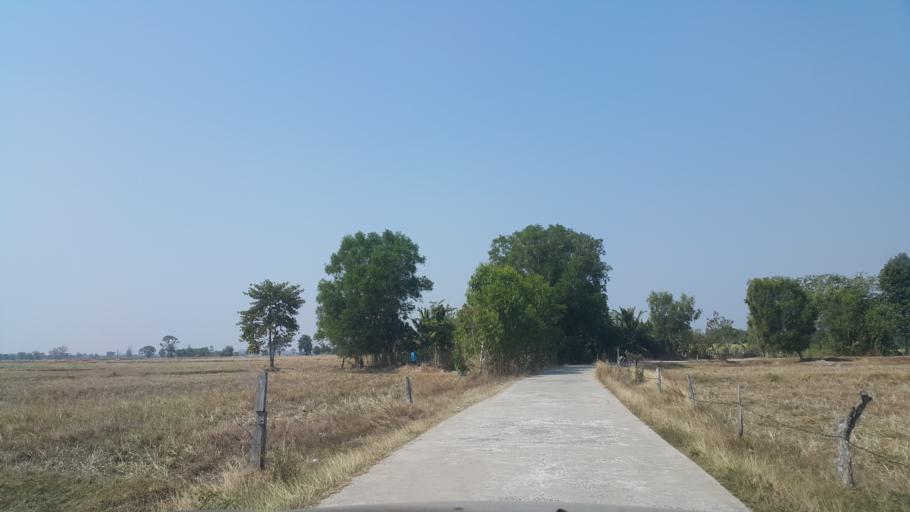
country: TH
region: Buriram
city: Krasang
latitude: 15.0904
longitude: 103.3822
